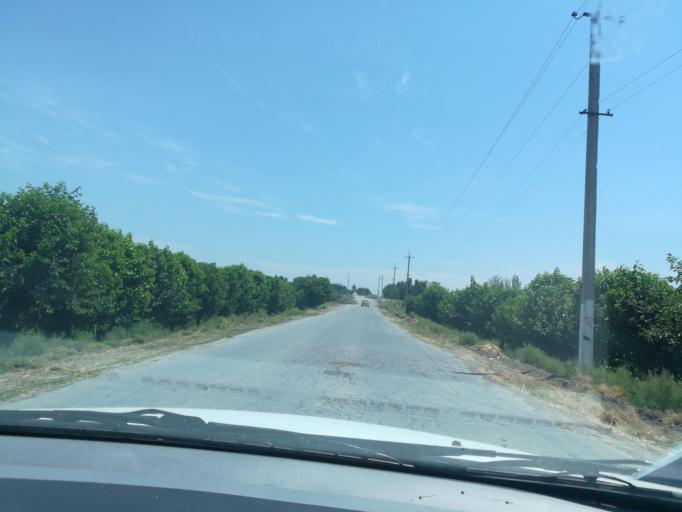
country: UZ
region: Namangan
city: Haqqulobod
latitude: 40.9000
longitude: 72.0006
